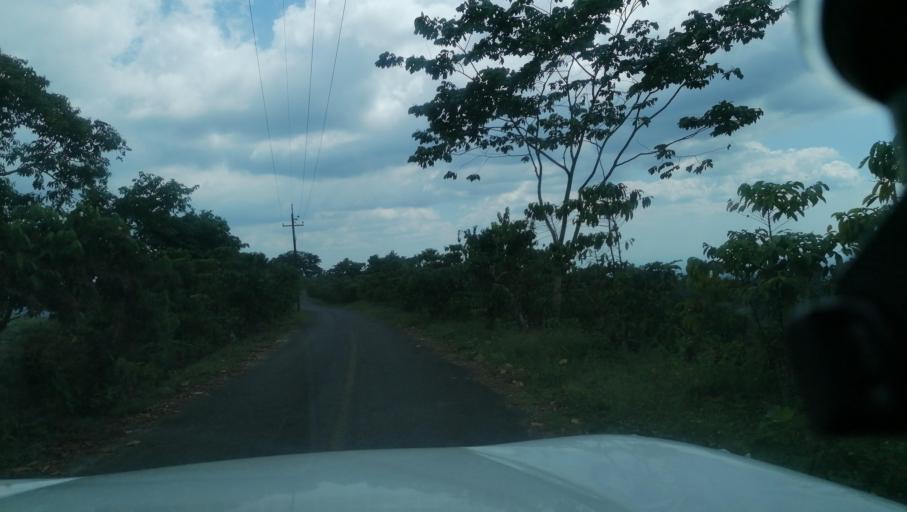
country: MX
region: Chiapas
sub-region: Cacahoatan
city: Benito Juarez
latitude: 15.0653
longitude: -92.1510
